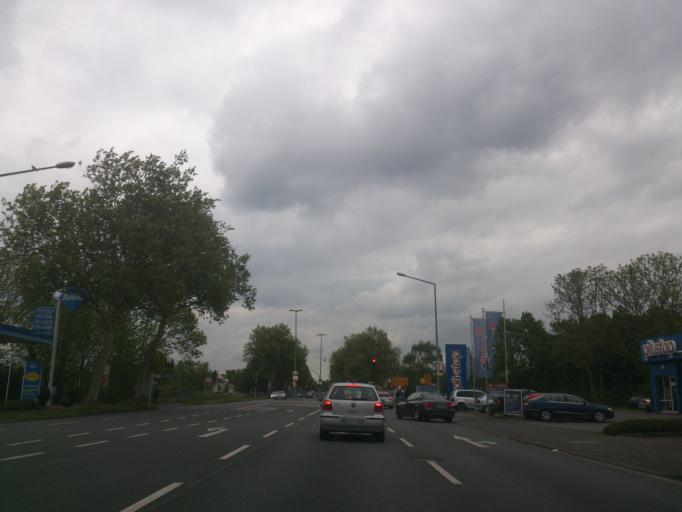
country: DE
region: North Rhine-Westphalia
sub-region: Regierungsbezirk Detmold
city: Paderborn
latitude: 51.7318
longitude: 8.7649
